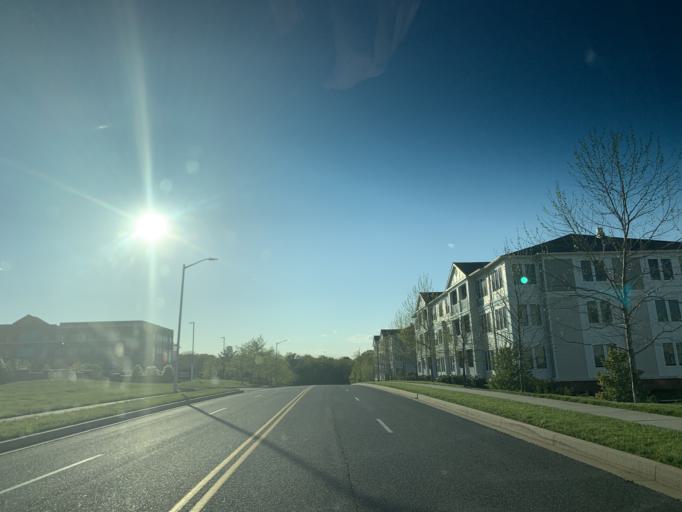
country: US
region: Maryland
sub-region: Harford County
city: Aberdeen
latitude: 39.5323
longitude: -76.1896
